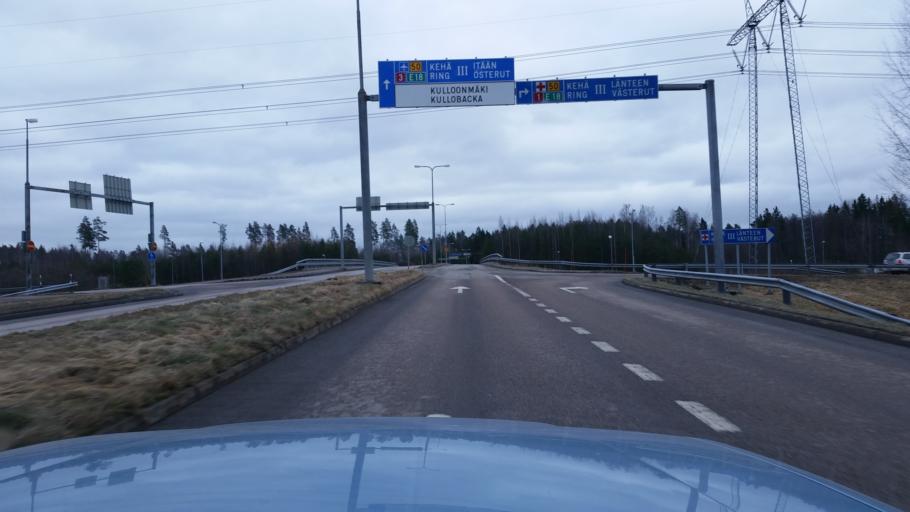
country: FI
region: Uusimaa
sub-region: Helsinki
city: Kauniainen
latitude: 60.2526
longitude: 24.7118
